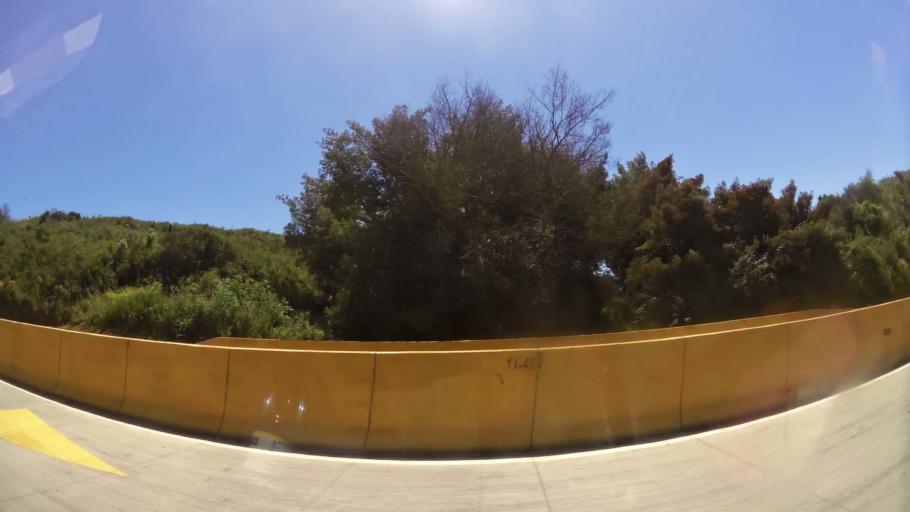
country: CL
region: Valparaiso
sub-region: Provincia de Valparaiso
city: Valparaiso
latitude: -33.0635
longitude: -71.6418
